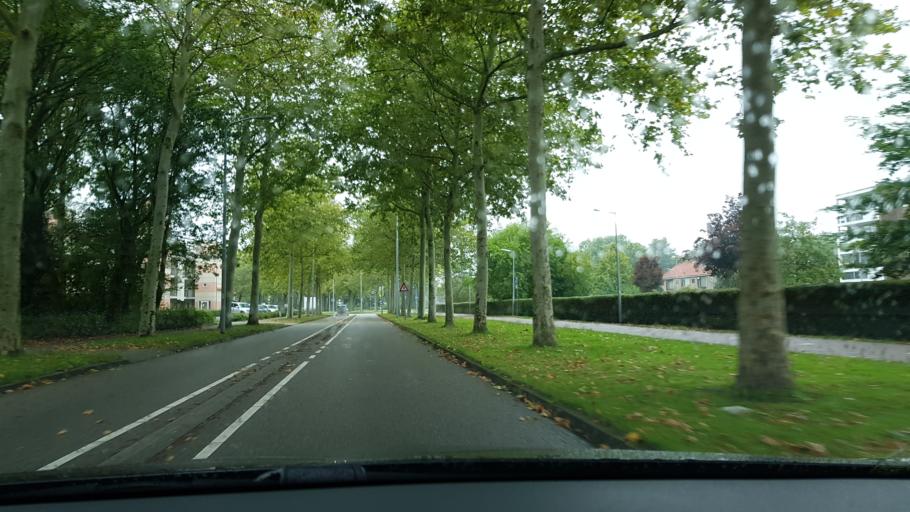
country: NL
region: North Holland
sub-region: Gemeente Haarlemmermeer
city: Hoofddorp
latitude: 52.3091
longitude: 4.6921
